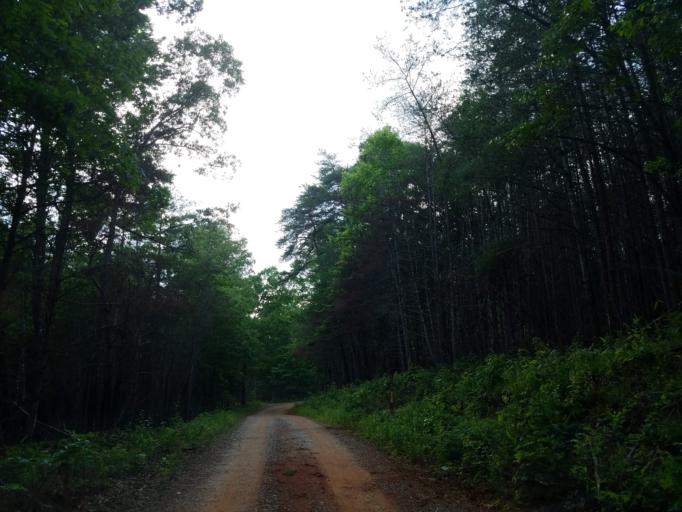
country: US
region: Georgia
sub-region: Lumpkin County
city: Dahlonega
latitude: 34.5857
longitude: -84.1241
